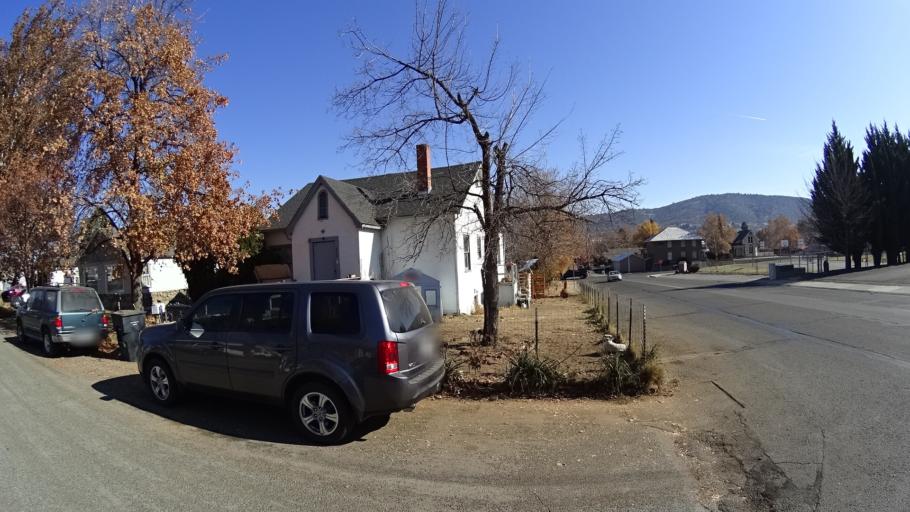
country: US
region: California
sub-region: Siskiyou County
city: Yreka
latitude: 41.7388
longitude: -122.6370
